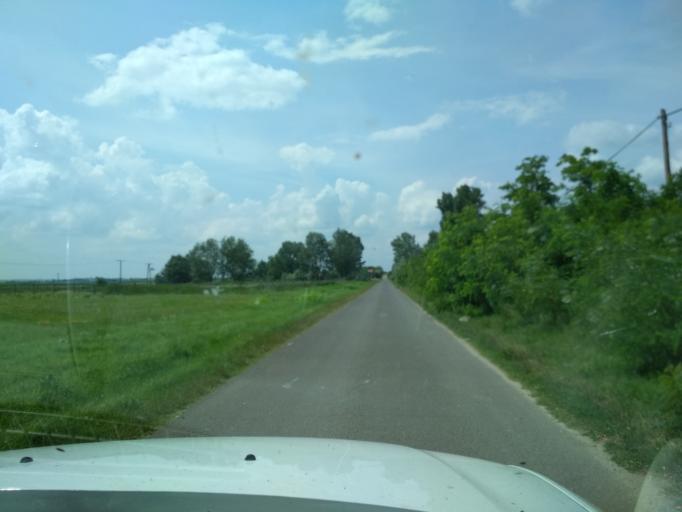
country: HU
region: Pest
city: Tapioszentmarton
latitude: 47.3244
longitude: 19.7677
